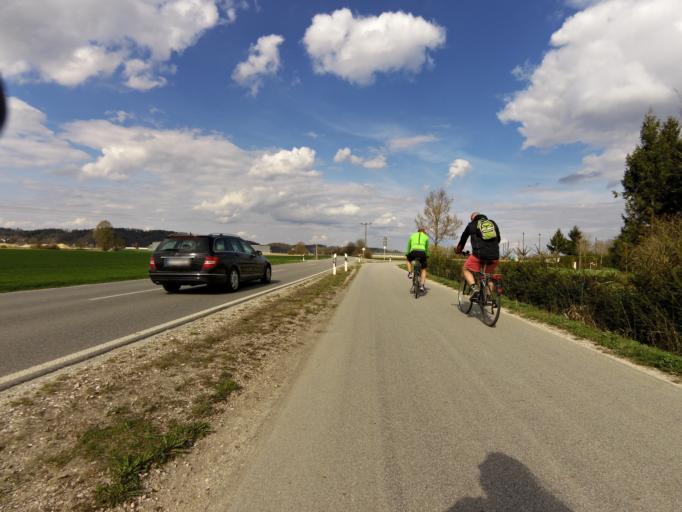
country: DE
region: Bavaria
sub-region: Lower Bavaria
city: Eching
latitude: 48.5243
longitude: 12.0591
